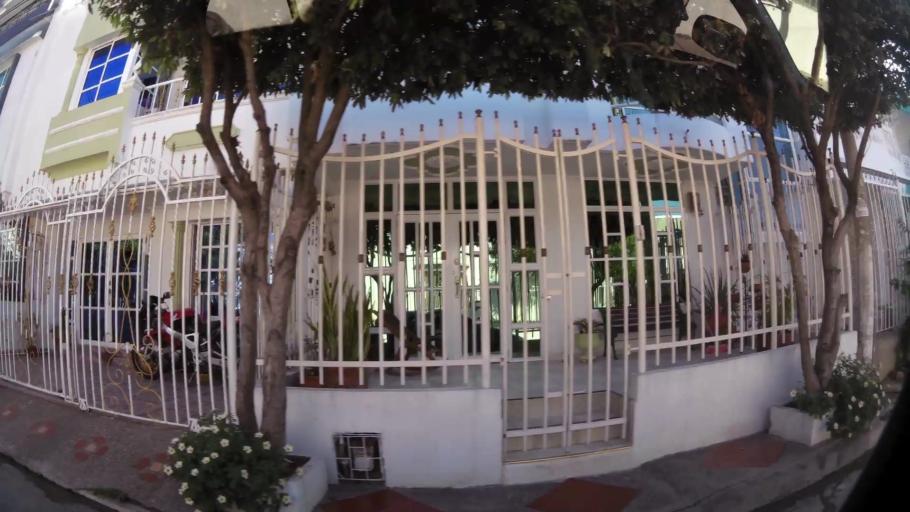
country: CO
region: Bolivar
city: Cartagena
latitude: 10.3914
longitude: -75.4981
